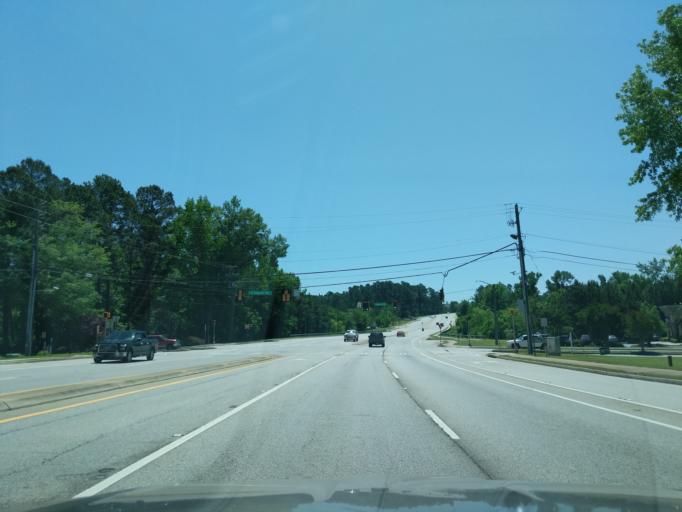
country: US
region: Georgia
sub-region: Columbia County
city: Martinez
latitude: 33.5403
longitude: -82.0817
